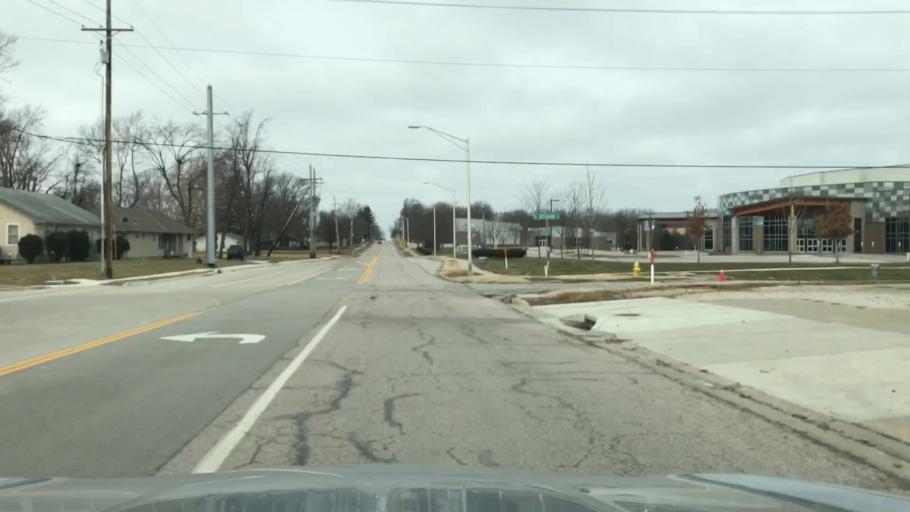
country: US
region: Missouri
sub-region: Jackson County
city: Lees Summit
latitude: 38.8962
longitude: -94.3770
